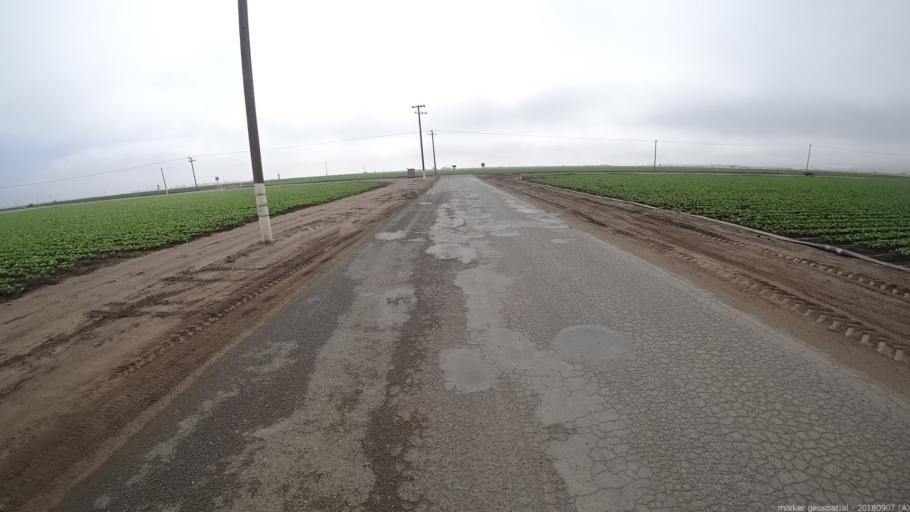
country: US
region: California
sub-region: Monterey County
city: Salinas
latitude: 36.6387
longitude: -121.6386
